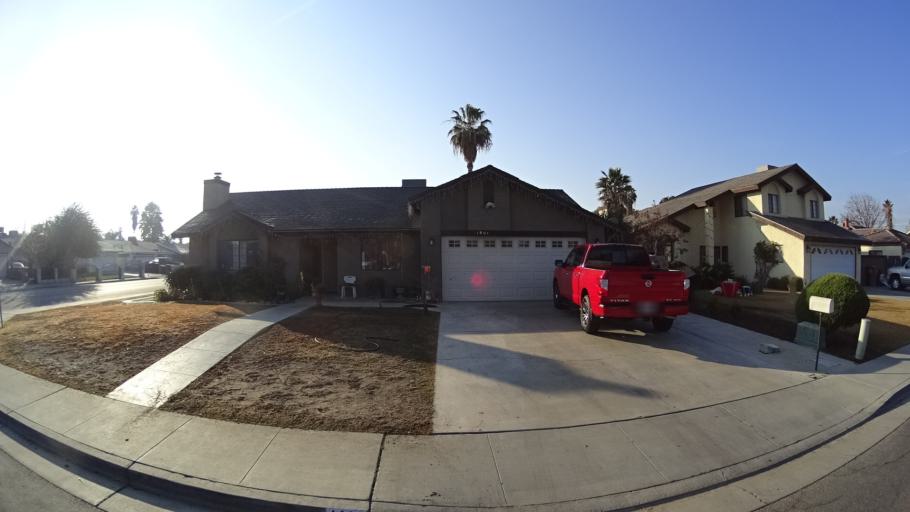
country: US
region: California
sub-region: Kern County
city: Greenfield
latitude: 35.2995
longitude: -119.0238
